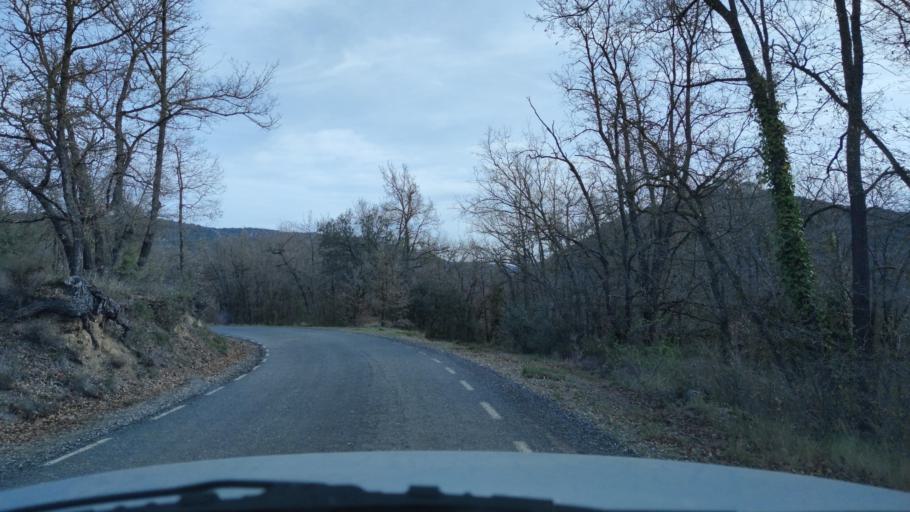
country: ES
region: Catalonia
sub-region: Provincia de Lleida
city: Camarasa
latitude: 41.8929
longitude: 0.8015
